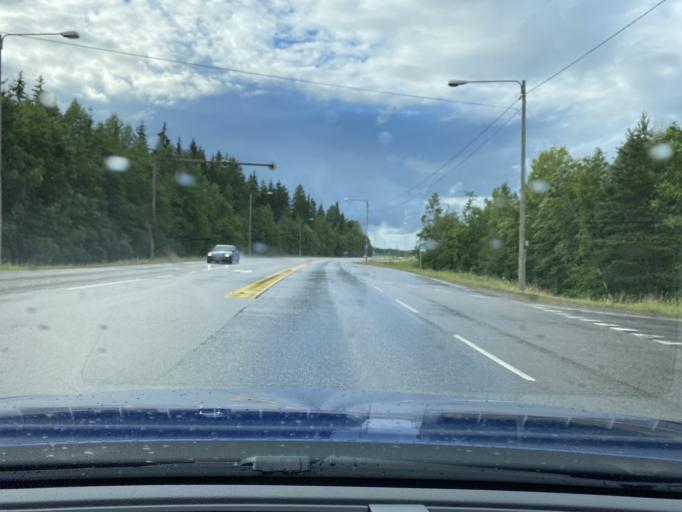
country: FI
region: Uusimaa
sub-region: Helsinki
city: Nurmijaervi
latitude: 60.5160
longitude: 24.8437
